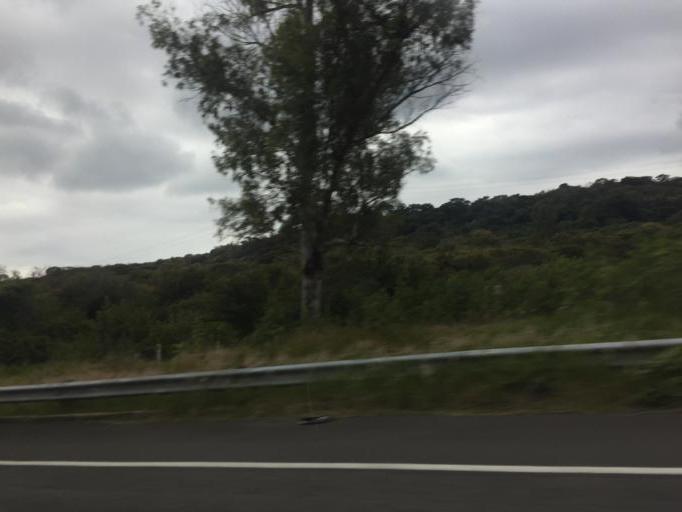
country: MX
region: Jalisco
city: Ocotlan
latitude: 20.4285
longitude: -102.7779
